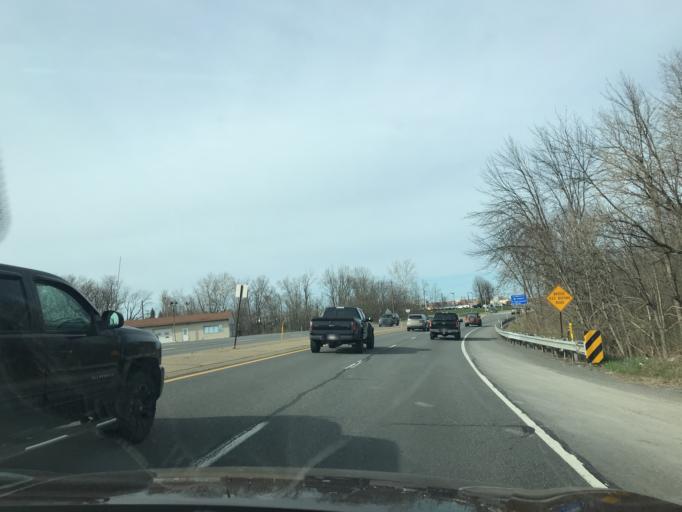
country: US
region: Pennsylvania
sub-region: Union County
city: Lewisburg
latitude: 40.9705
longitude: -76.8927
